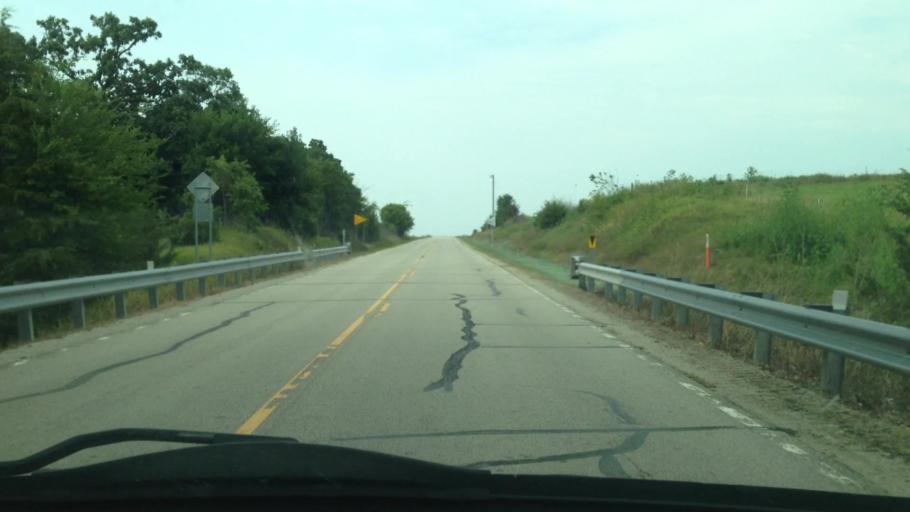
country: US
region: Minnesota
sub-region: Fillmore County
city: Preston
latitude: 43.7703
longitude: -91.9498
